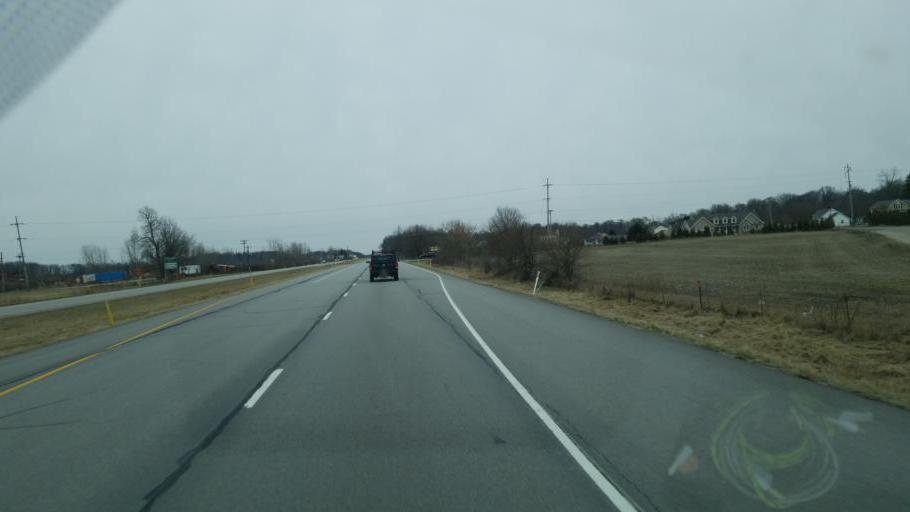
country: US
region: Indiana
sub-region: Marshall County
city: Plymouth
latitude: 41.3195
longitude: -86.2758
